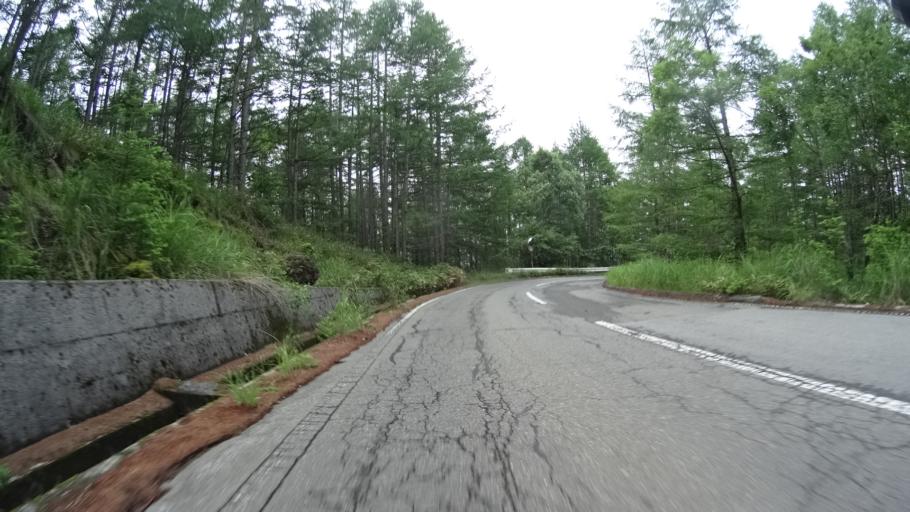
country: JP
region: Nagano
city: Chino
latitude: 36.0504
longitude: 138.3143
